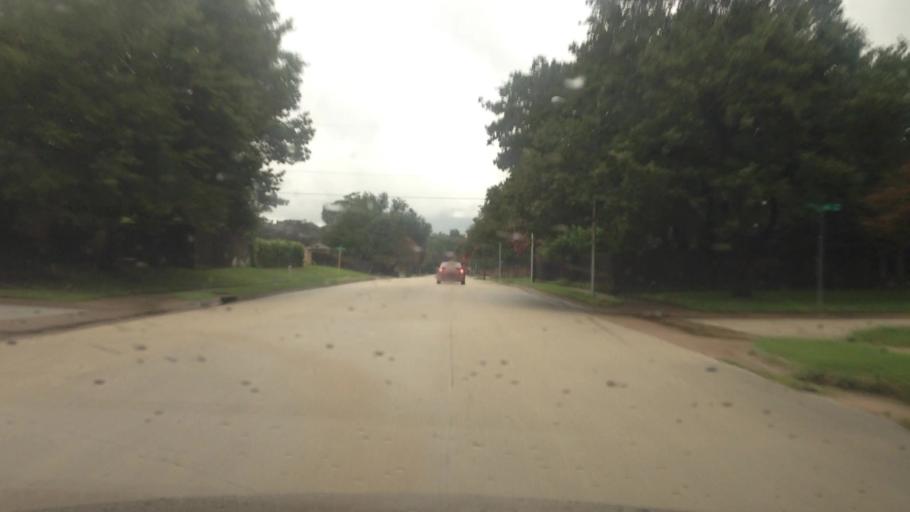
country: US
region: Texas
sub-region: Tarrant County
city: Colleyville
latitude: 32.8719
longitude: -97.1700
